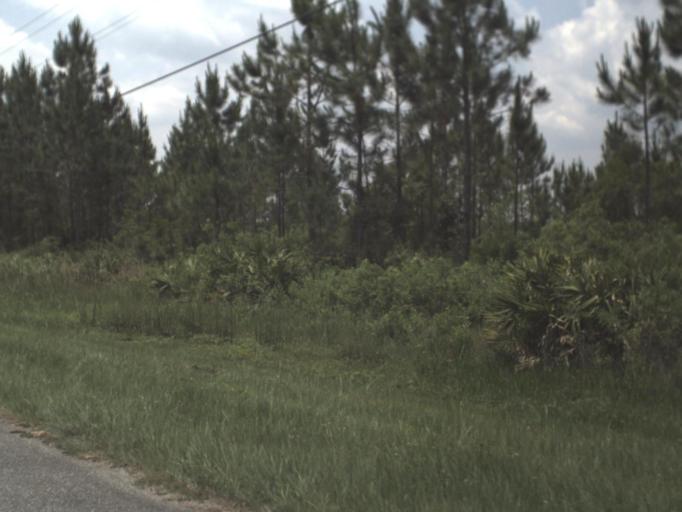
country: US
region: Florida
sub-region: Putnam County
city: Palatka
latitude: 29.5885
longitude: -81.7155
